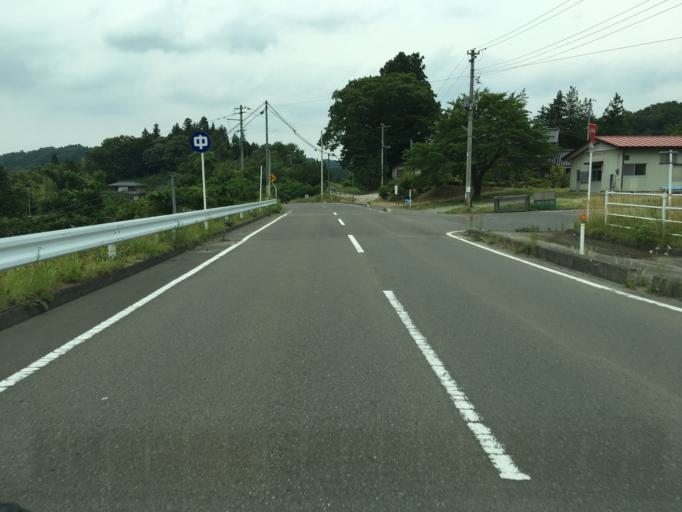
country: JP
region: Fukushima
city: Nihommatsu
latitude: 37.6125
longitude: 140.5599
